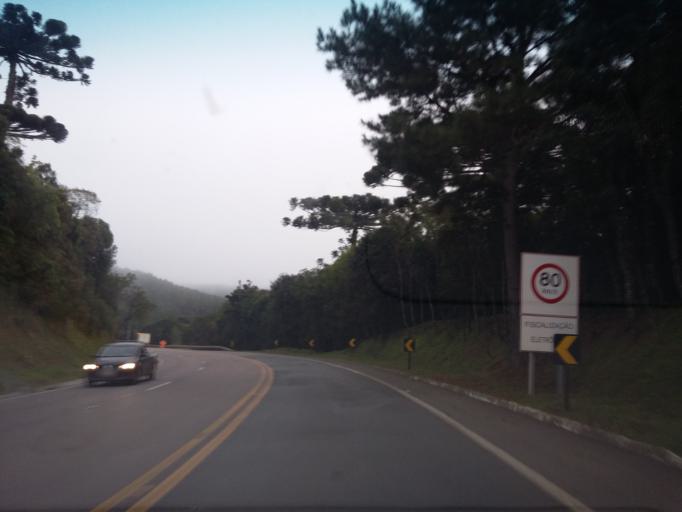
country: BR
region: Santa Catarina
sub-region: Curitibanos
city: Curitibanos
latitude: -27.2198
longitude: -50.4622
